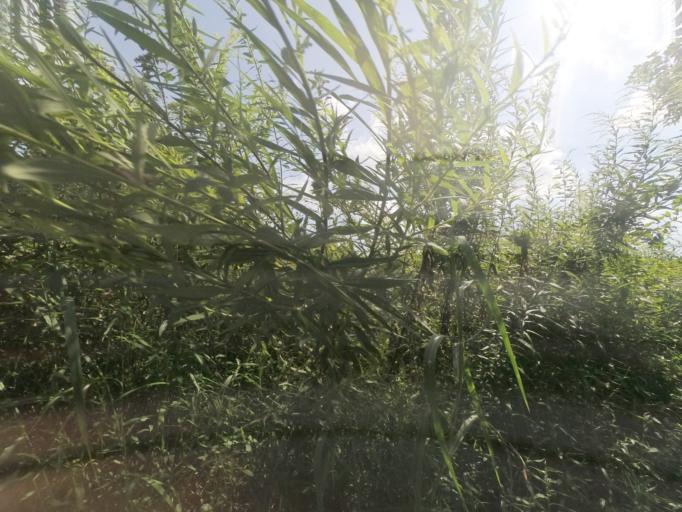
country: US
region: Ohio
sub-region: Lawrence County
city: Burlington
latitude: 38.3839
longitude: -82.5133
